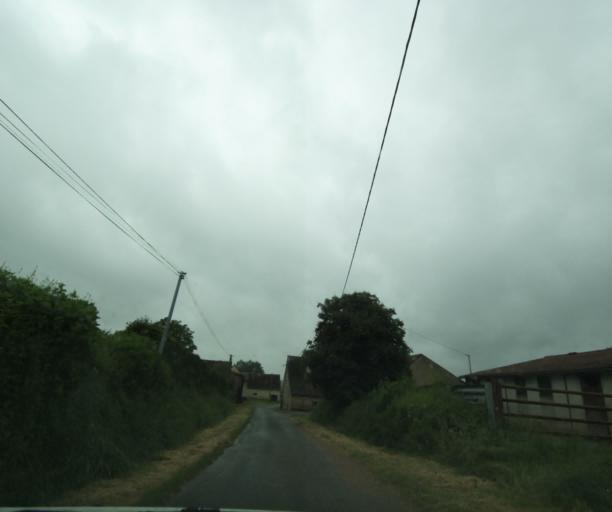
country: FR
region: Bourgogne
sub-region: Departement de Saone-et-Loire
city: Palinges
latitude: 46.5144
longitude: 4.2062
